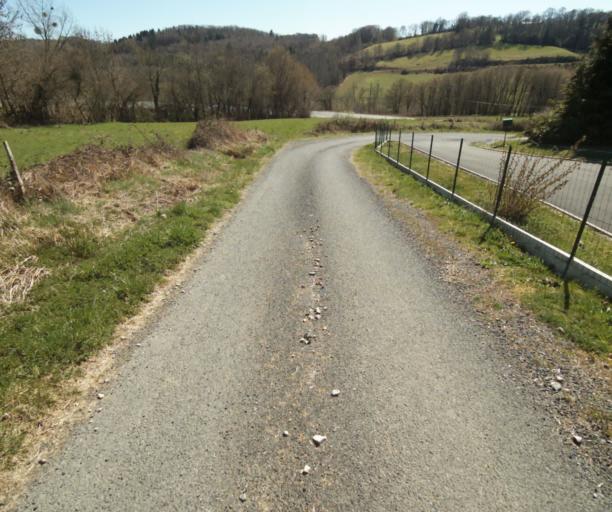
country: FR
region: Limousin
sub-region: Departement de la Correze
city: Chamboulive
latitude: 45.4418
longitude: 1.7228
